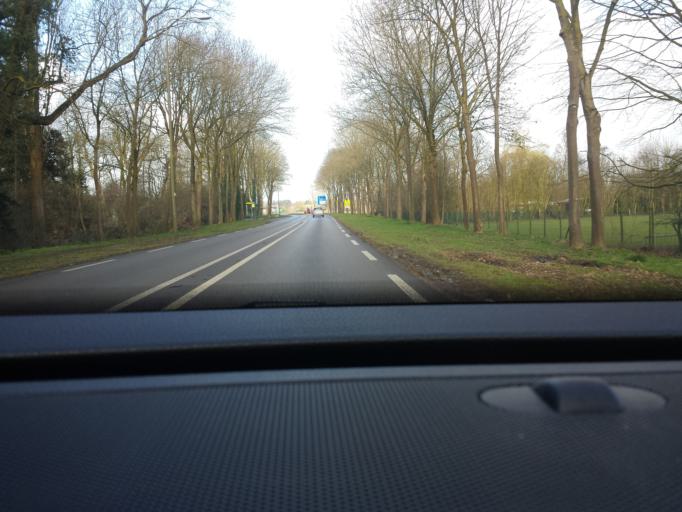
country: NL
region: Gelderland
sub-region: Gemeente Zutphen
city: Warnsveld
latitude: 52.1447
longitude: 6.2256
